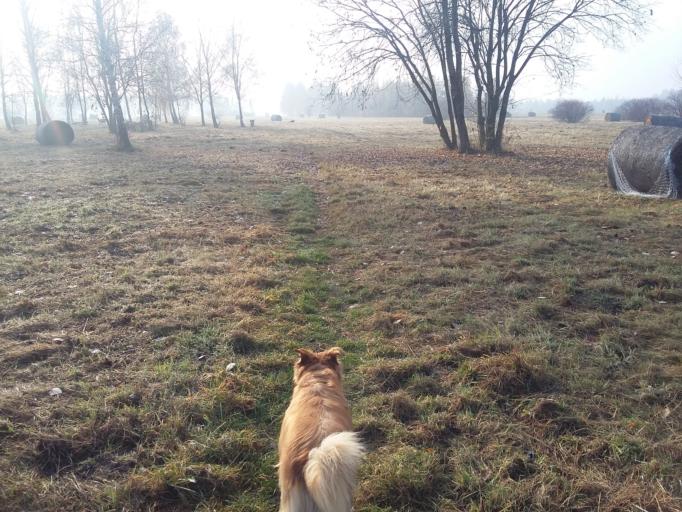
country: PL
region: Lodz Voivodeship
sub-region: Powiat pabianicki
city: Ksawerow
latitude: 51.7347
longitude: 19.3885
